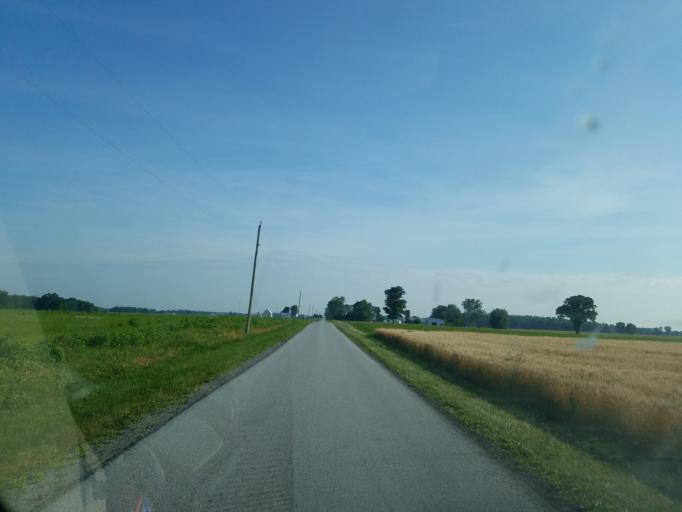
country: US
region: Ohio
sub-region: Hardin County
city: Kenton
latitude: 40.7624
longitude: -83.6714
